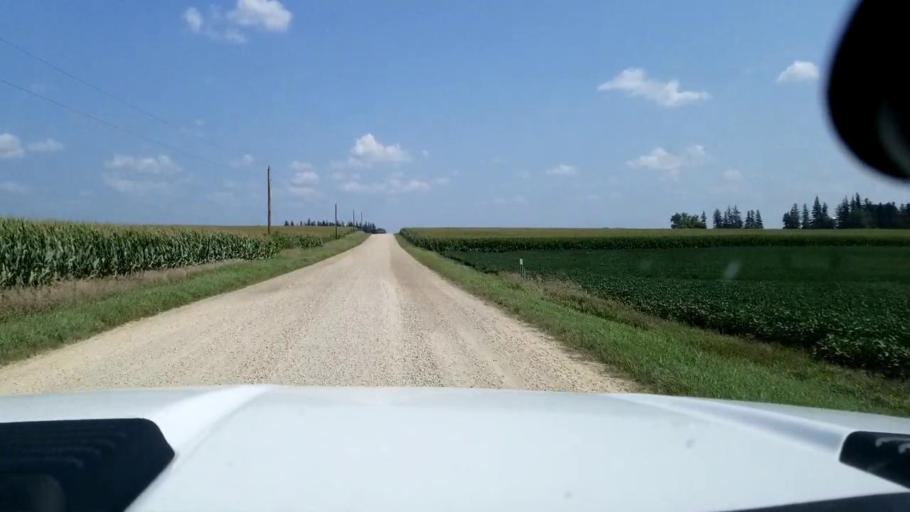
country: US
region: Minnesota
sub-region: Goodhue County
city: Kenyon
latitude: 44.3416
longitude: -92.8980
